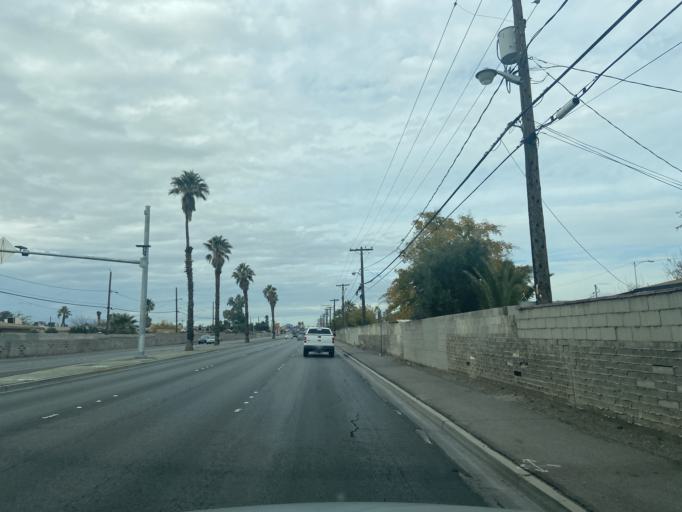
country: US
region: Nevada
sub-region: Clark County
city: Las Vegas
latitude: 36.1855
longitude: -115.1831
